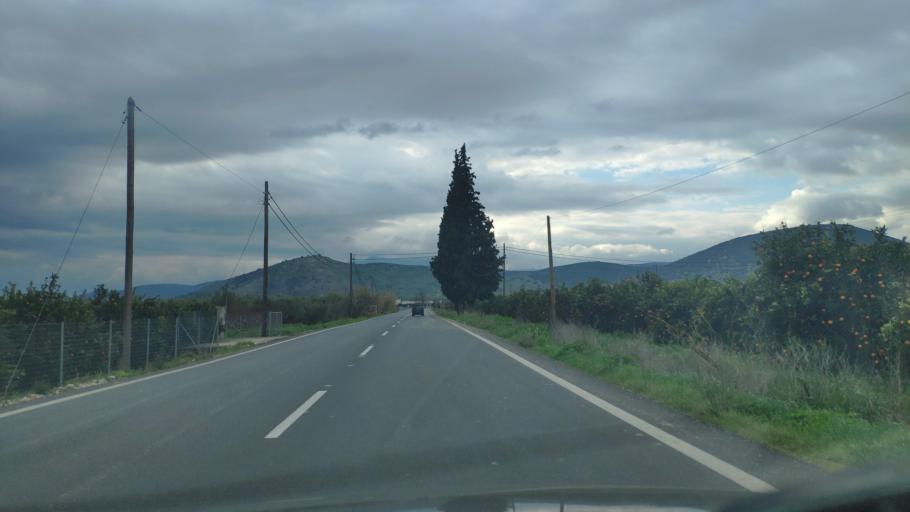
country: GR
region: Peloponnese
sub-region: Nomos Argolidos
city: Nea Kios
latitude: 37.5754
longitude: 22.7084
